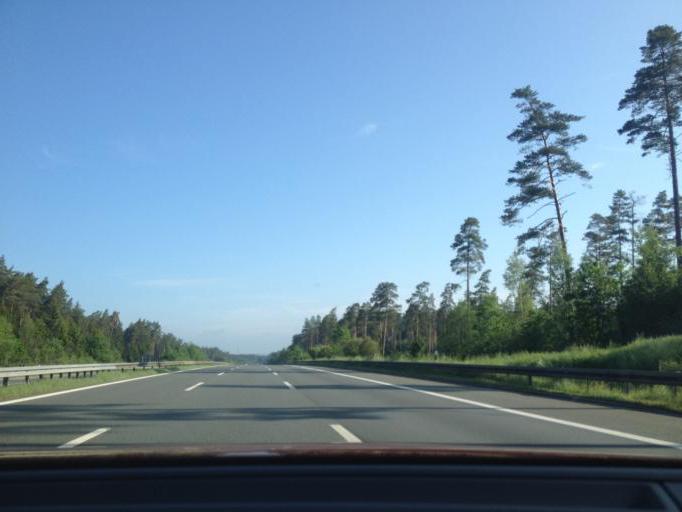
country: DE
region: Bavaria
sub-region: Regierungsbezirk Mittelfranken
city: Velden
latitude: 49.6819
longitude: 11.4674
